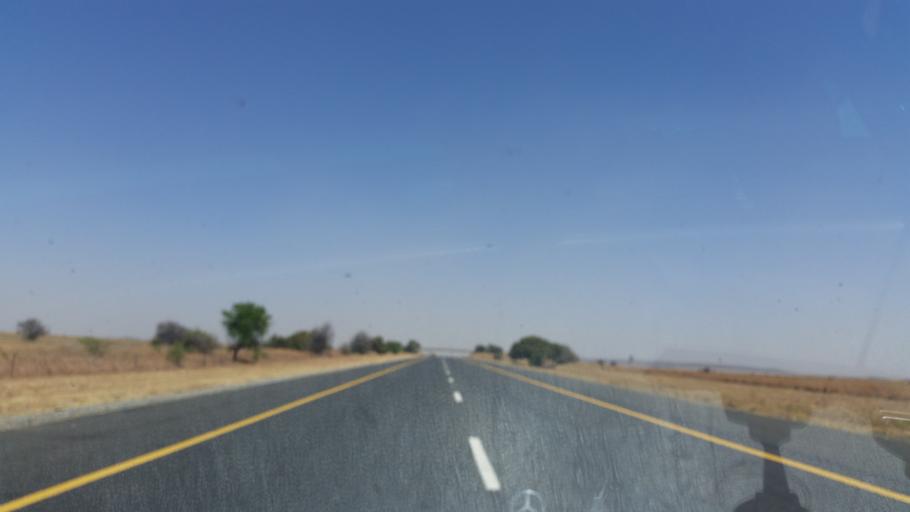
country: ZA
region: Orange Free State
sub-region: Lejweleputswa District Municipality
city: Winburg
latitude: -28.6503
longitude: 26.8759
